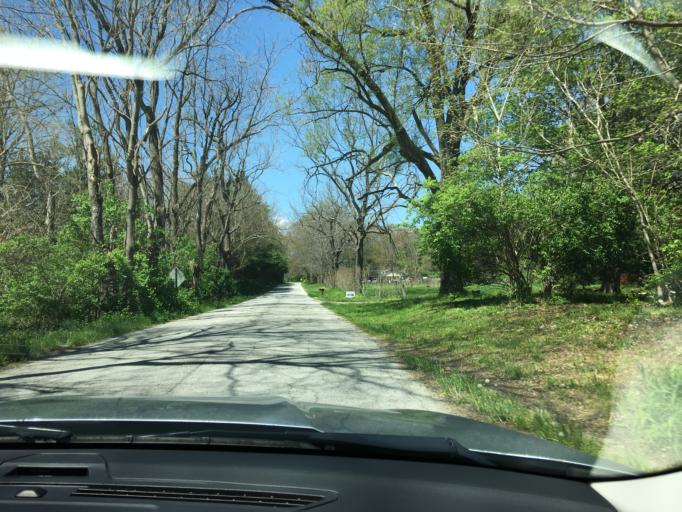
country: US
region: Indiana
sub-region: Tippecanoe County
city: Dayton
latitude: 40.3149
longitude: -86.7531
